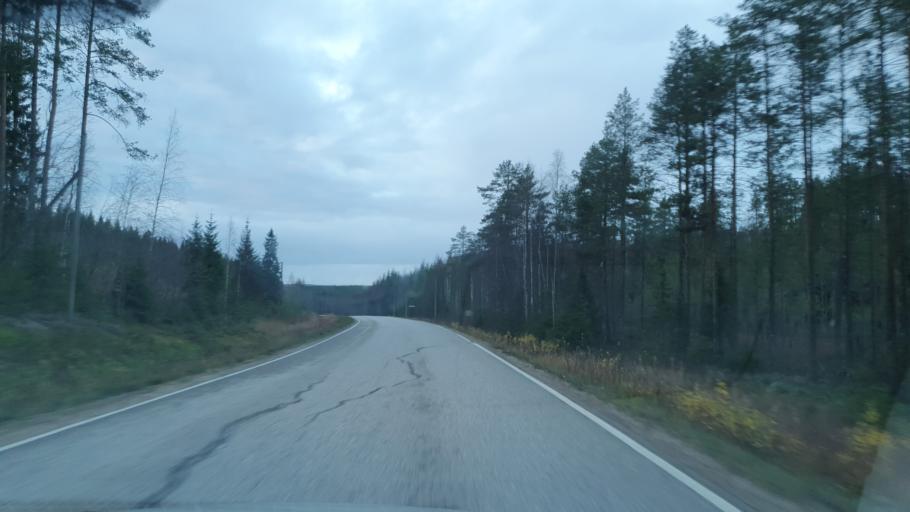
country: FI
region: Kainuu
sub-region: Kajaani
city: Ristijaervi
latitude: 64.4255
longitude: 28.3950
